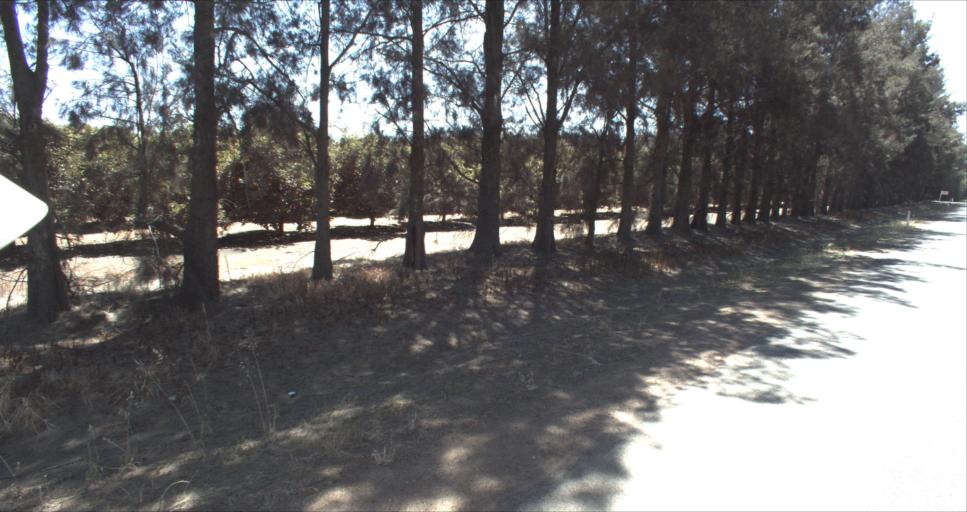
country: AU
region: New South Wales
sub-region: Leeton
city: Leeton
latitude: -34.5301
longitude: 146.3292
